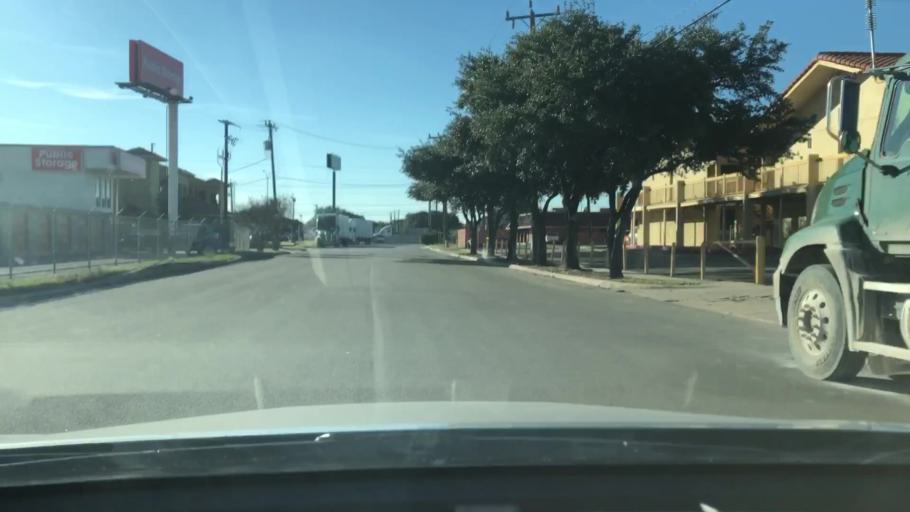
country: US
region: Texas
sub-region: Bexar County
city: Kirby
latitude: 29.4881
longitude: -98.4003
